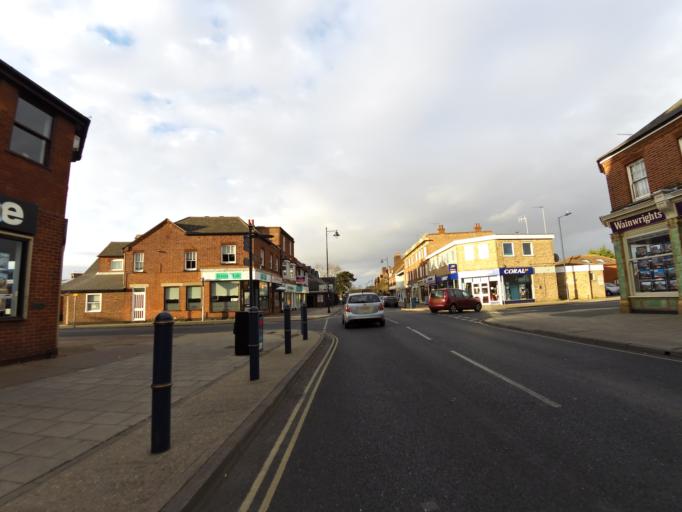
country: GB
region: England
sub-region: Suffolk
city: Felixstowe
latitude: 51.9659
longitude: 1.3525
